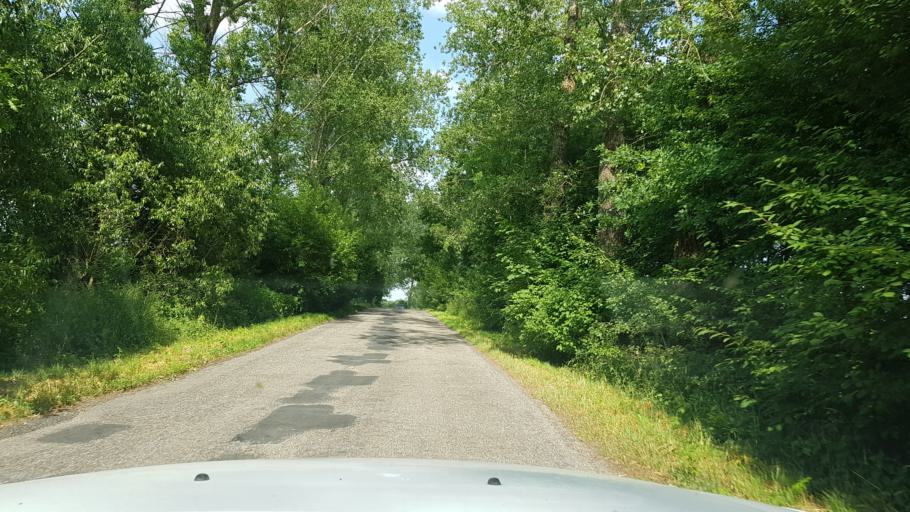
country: PL
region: West Pomeranian Voivodeship
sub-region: Powiat goleniowski
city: Osina
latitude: 53.5941
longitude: 14.9942
